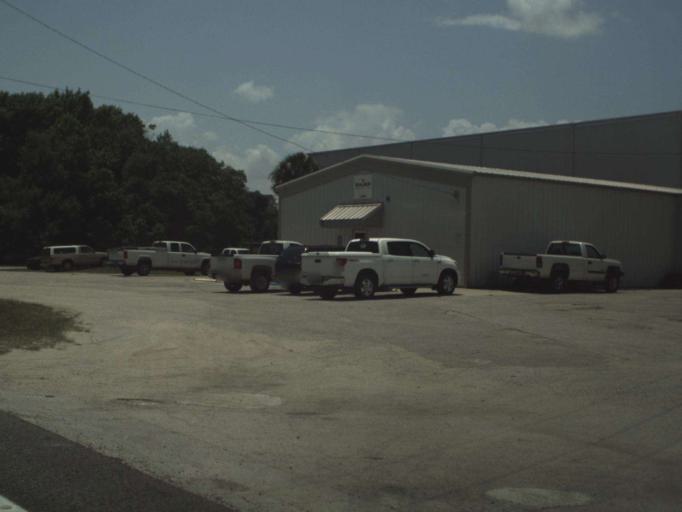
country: US
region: Florida
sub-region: Volusia County
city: Oak Hill
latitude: 28.8080
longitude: -80.8718
